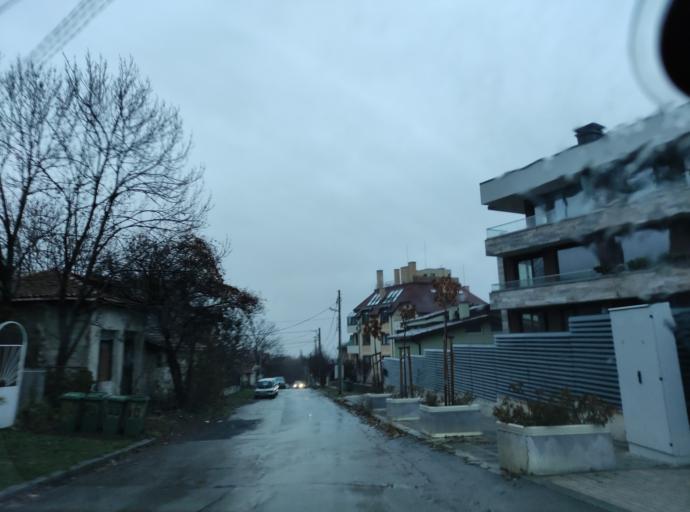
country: BG
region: Sofia-Capital
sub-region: Stolichna Obshtina
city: Sofia
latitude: 42.6311
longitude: 23.3120
